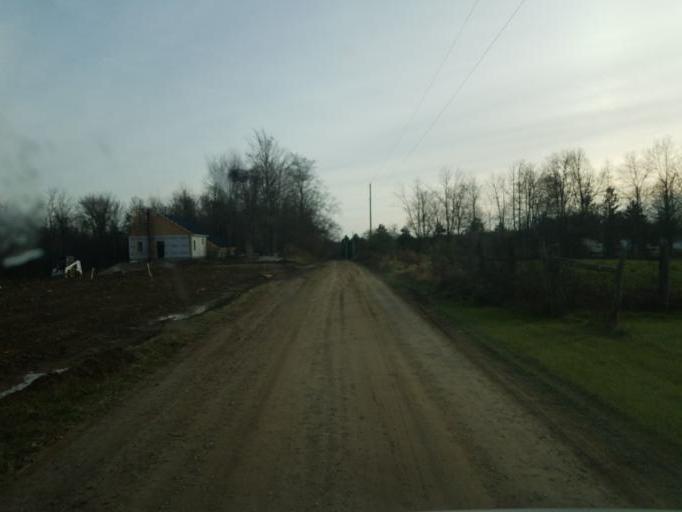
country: US
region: Ohio
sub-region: Richland County
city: Lexington
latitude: 40.5751
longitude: -82.6764
